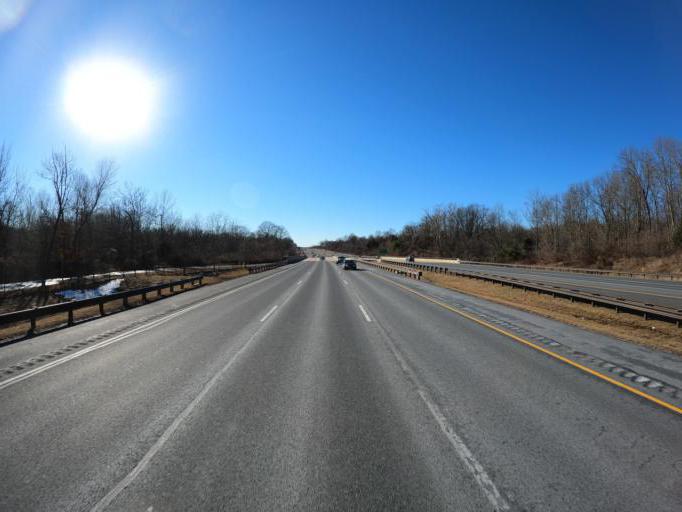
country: US
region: Maryland
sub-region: Montgomery County
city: Rossmoor
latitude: 39.1257
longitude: -77.0989
